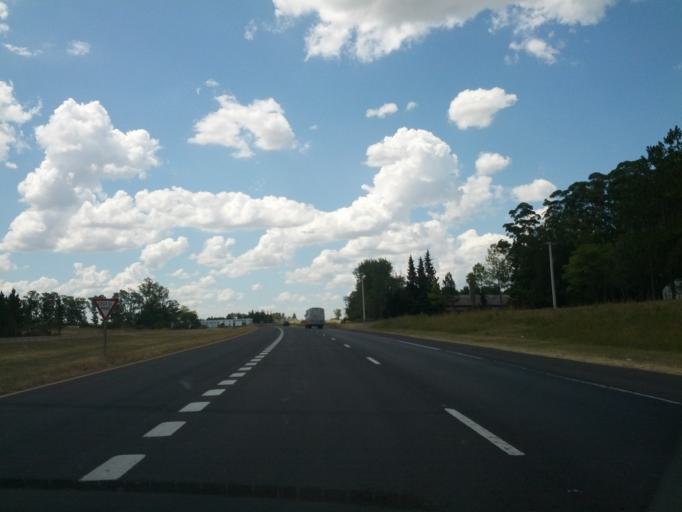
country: AR
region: Entre Rios
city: Concepcion del Uruguay
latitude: -32.5019
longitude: -58.3157
